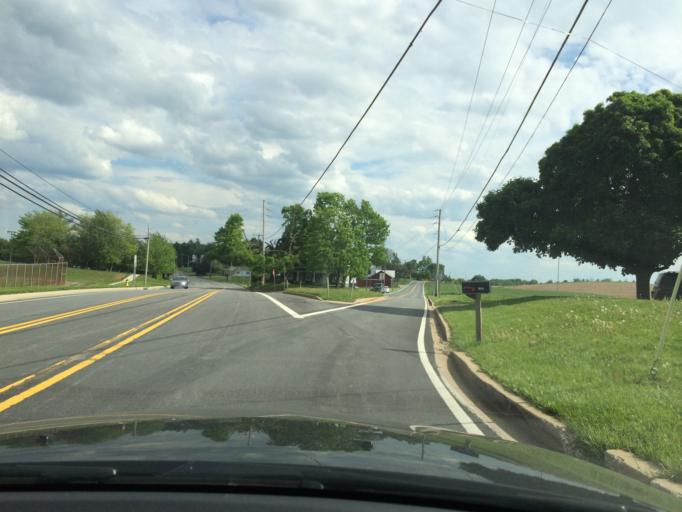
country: US
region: Maryland
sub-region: Carroll County
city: Westminster
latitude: 39.5281
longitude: -76.9931
